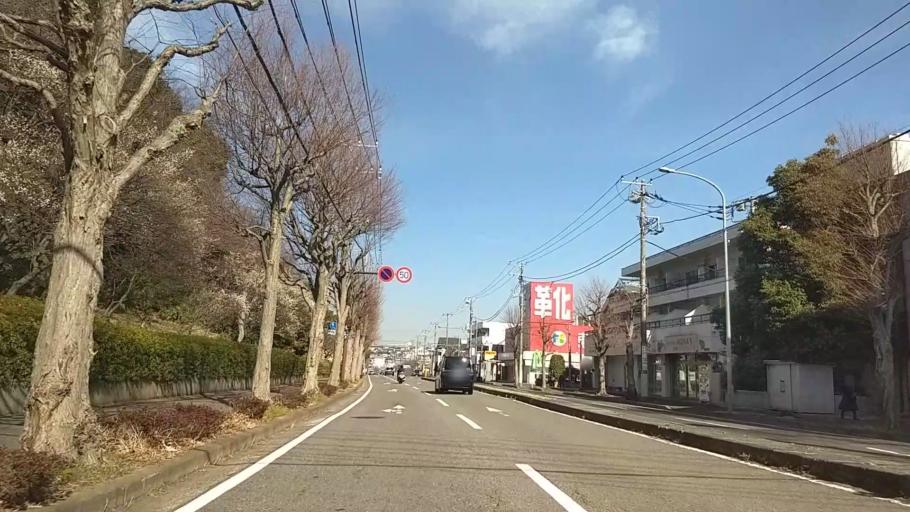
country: JP
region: Kanagawa
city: Kamakura
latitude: 35.3759
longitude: 139.5815
